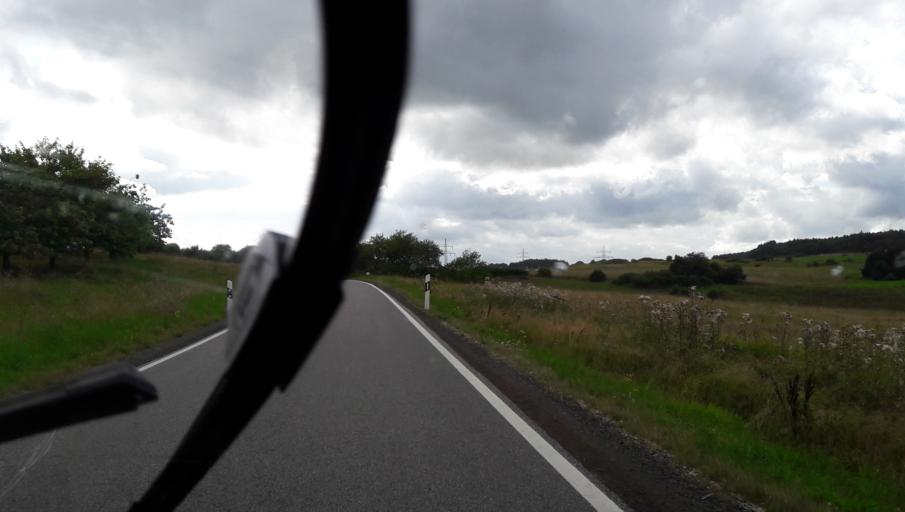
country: DE
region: Saarland
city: Nohfelden
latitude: 49.5614
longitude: 7.1608
